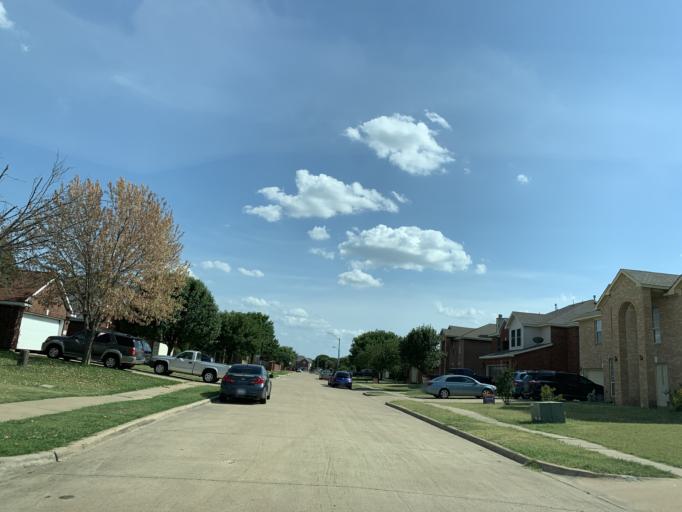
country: US
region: Texas
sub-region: Dallas County
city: Cedar Hill
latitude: 32.6512
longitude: -97.0085
